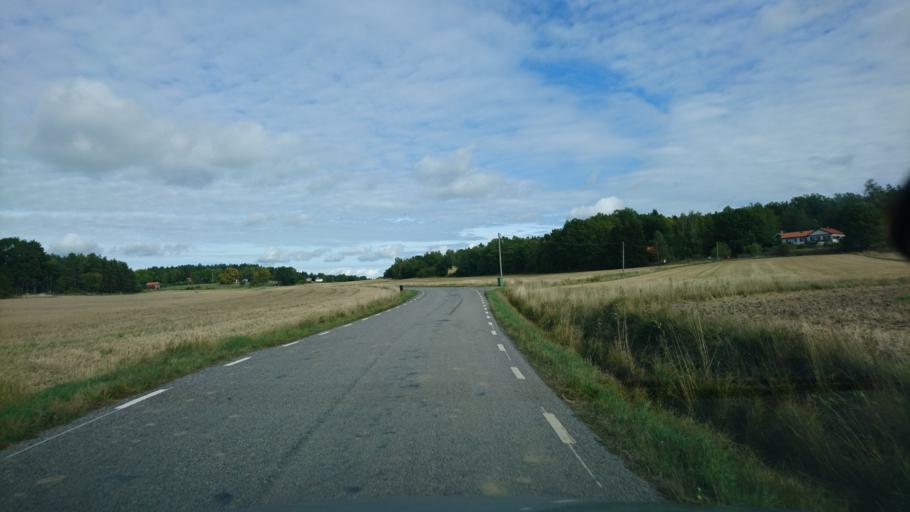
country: SE
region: Soedermanland
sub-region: Strangnas Kommun
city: Stallarholmen
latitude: 59.3821
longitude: 17.2608
